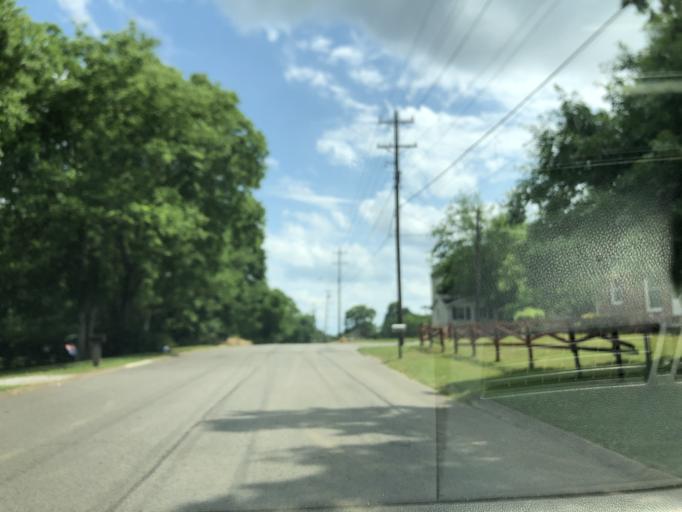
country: US
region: Tennessee
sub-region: Davidson County
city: Goodlettsville
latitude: 36.2695
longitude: -86.6950
